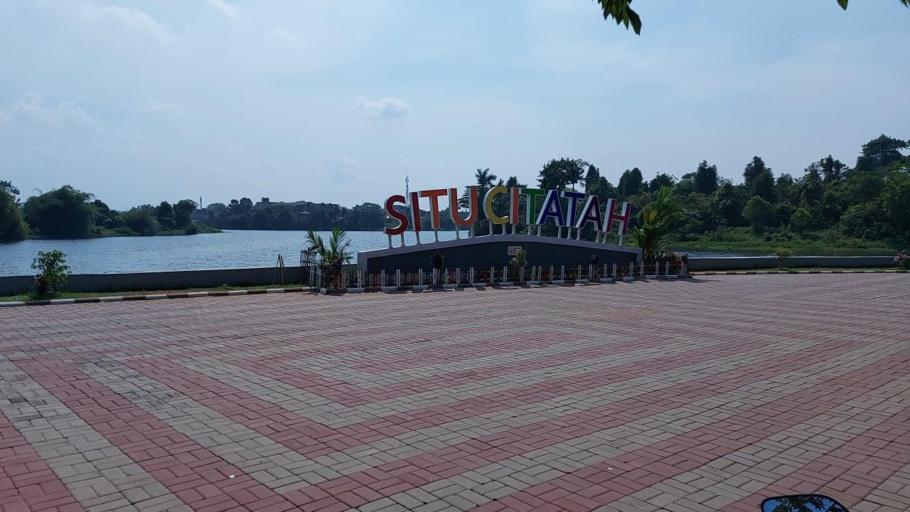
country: ID
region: West Java
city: Cibinong
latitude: -6.4708
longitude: 106.8552
